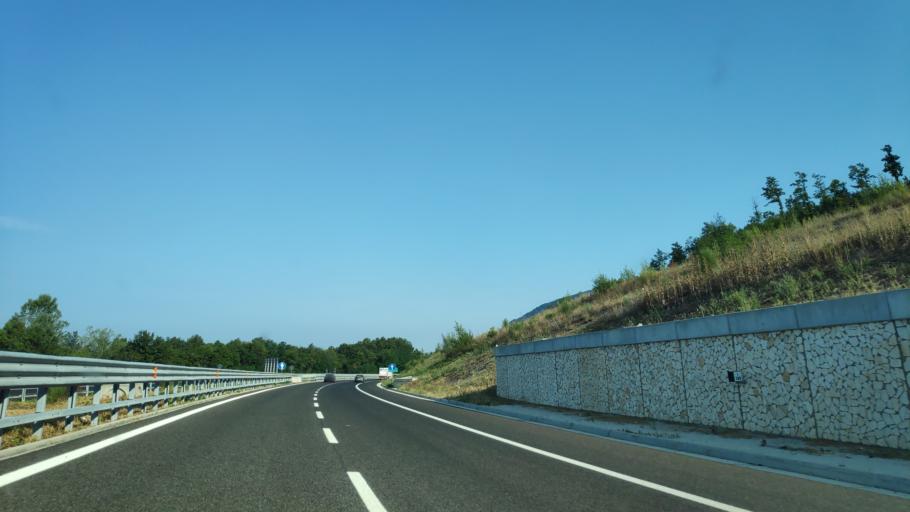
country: IT
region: Basilicate
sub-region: Provincia di Potenza
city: Nemoli
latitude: 40.1026
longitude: 15.7982
